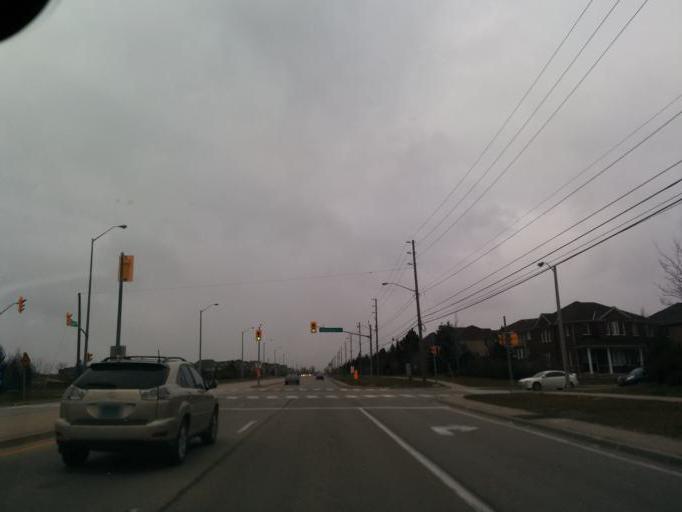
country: CA
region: Ontario
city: Brampton
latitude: 43.7479
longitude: -79.7725
